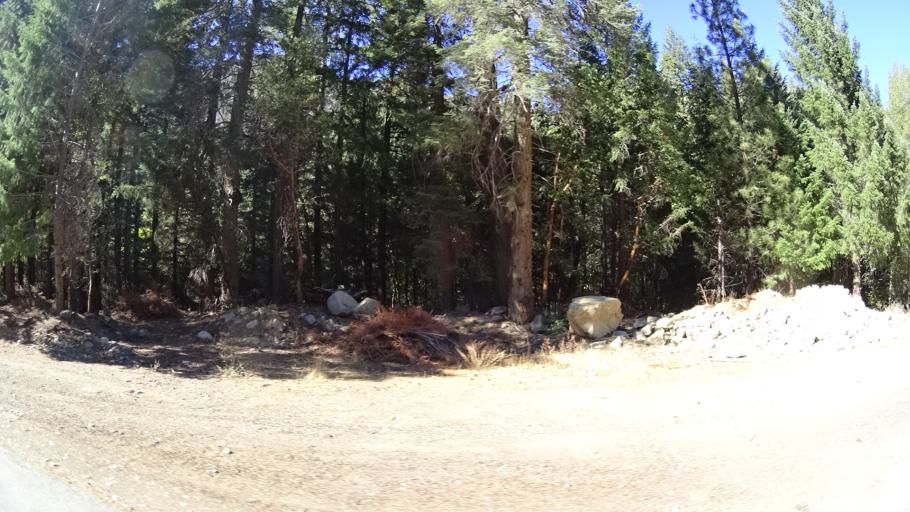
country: US
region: California
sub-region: Siskiyou County
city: Yreka
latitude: 41.3688
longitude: -123.0274
